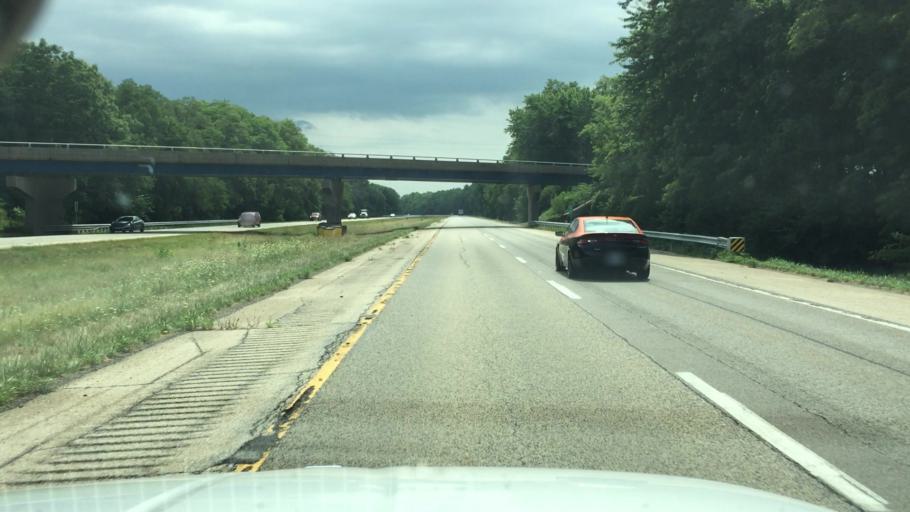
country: US
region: Illinois
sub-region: Peoria County
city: Hanna City
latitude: 40.8087
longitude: -89.8334
